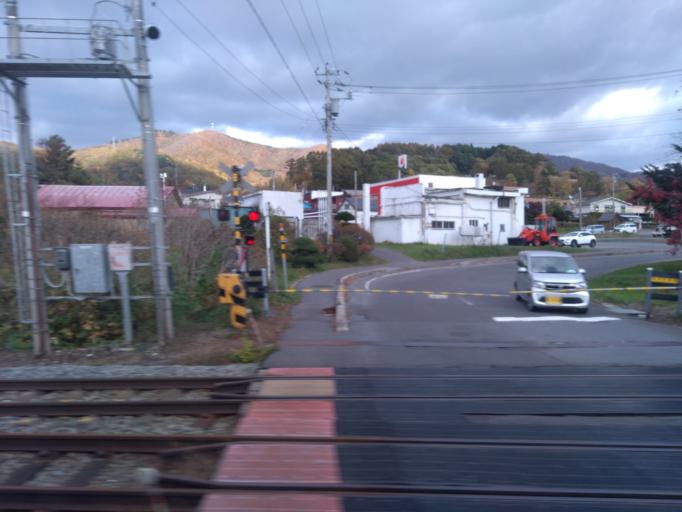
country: JP
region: Hokkaido
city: Date
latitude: 42.5823
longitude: 140.7136
